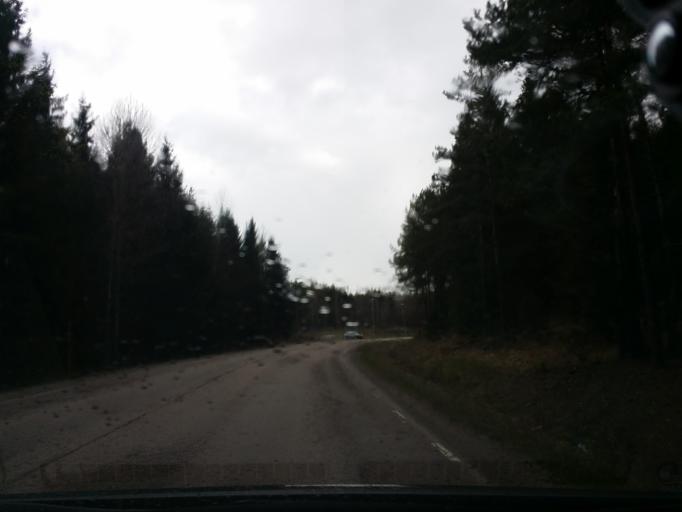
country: SE
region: Uppsala
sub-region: Enkopings Kommun
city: Enkoping
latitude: 59.6364
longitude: 17.1429
